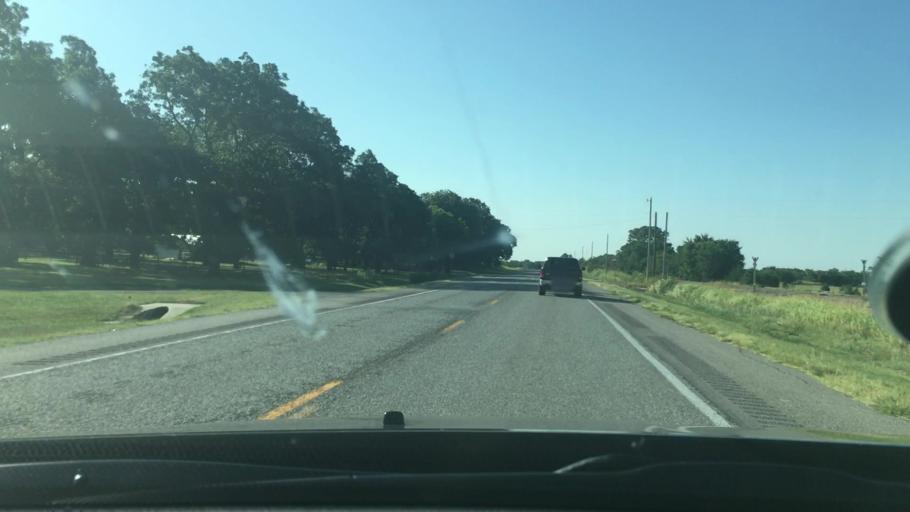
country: US
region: Oklahoma
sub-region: Johnston County
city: Tishomingo
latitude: 34.2606
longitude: -96.7692
